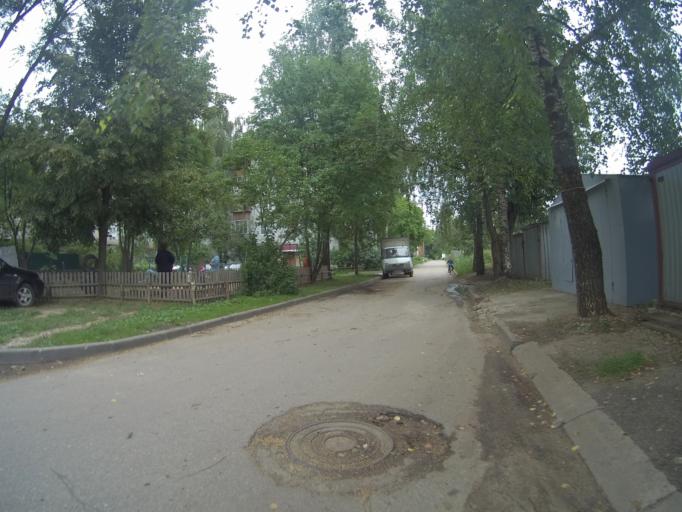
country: RU
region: Vladimir
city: Vladimir
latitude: 56.1287
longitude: 40.3676
